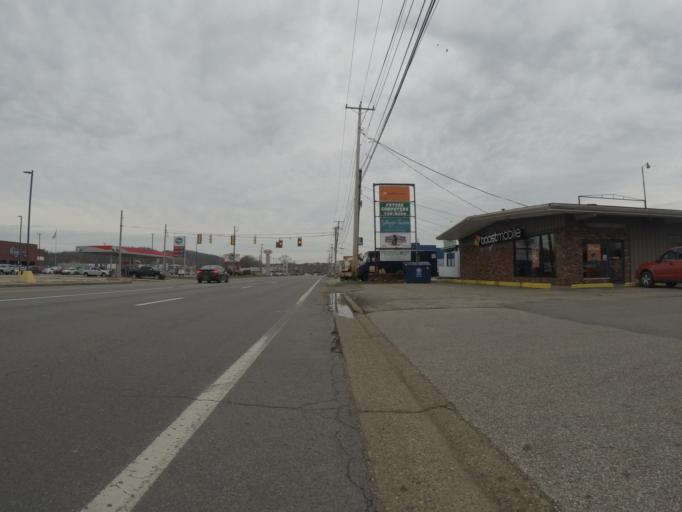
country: US
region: West Virginia
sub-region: Cabell County
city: Barboursville
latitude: 38.4142
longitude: -82.3032
